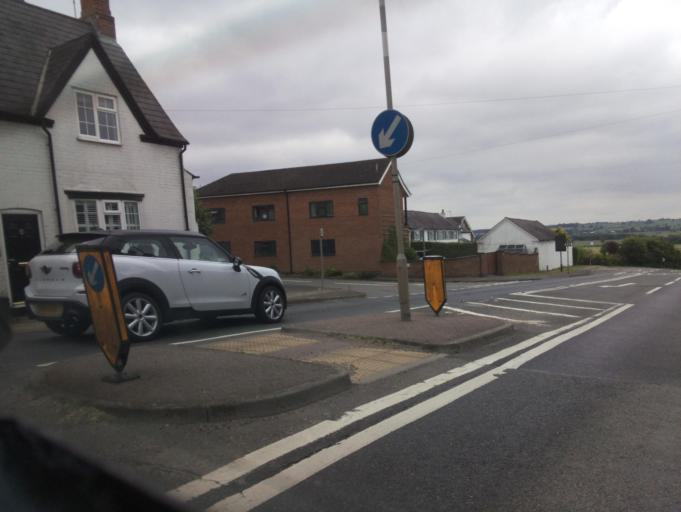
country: GB
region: England
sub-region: Leicestershire
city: Melton Mowbray
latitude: 52.7437
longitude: -0.8637
